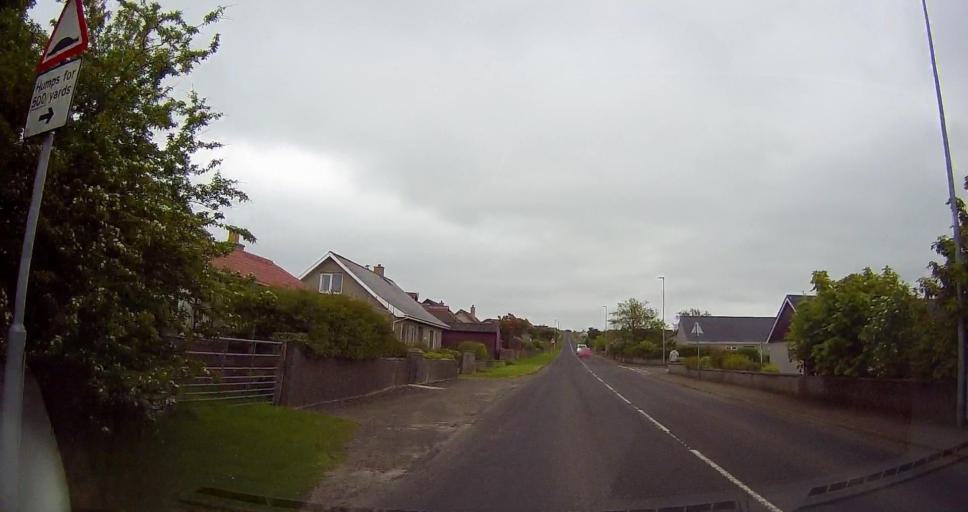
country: GB
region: Scotland
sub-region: Orkney Islands
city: Kirkwall
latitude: 58.9727
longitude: -2.9495
